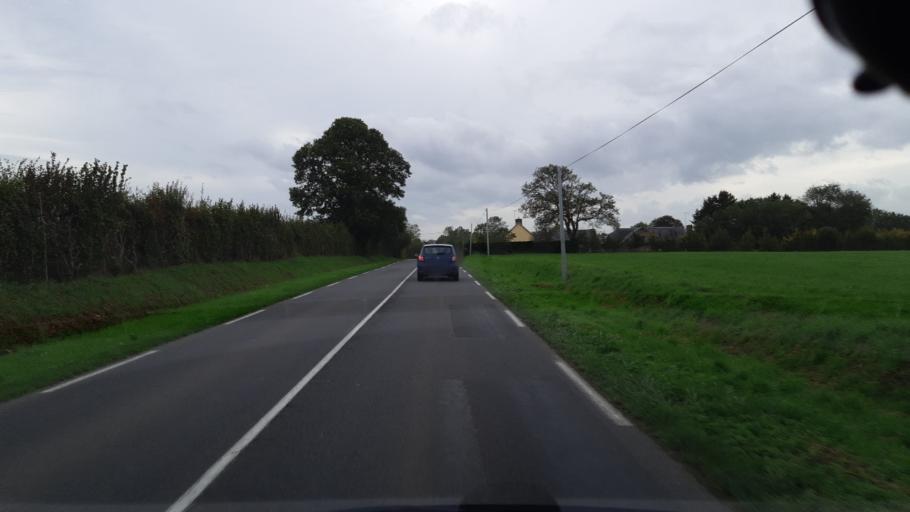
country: FR
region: Lower Normandy
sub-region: Departement de la Manche
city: Gavray
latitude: 48.9359
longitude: -1.3650
